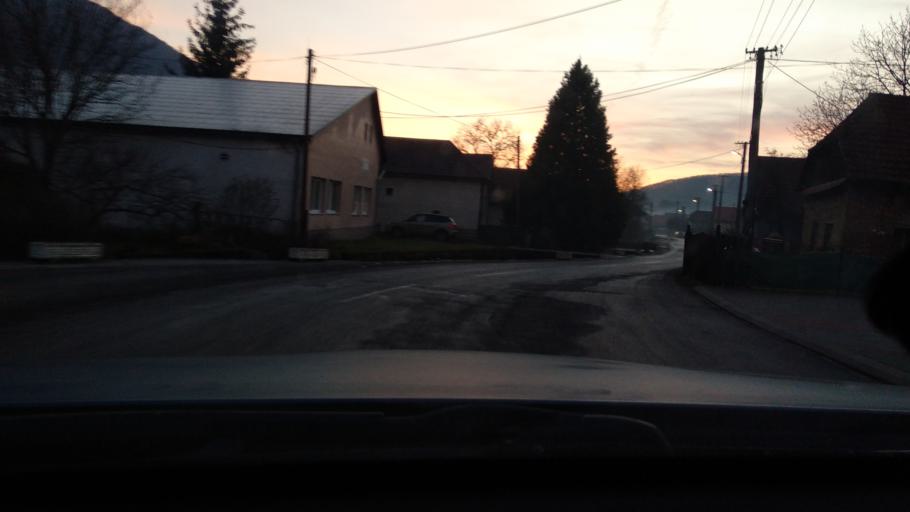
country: SK
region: Nitriansky
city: Banovce nad Bebravou
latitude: 48.8521
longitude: 18.2954
